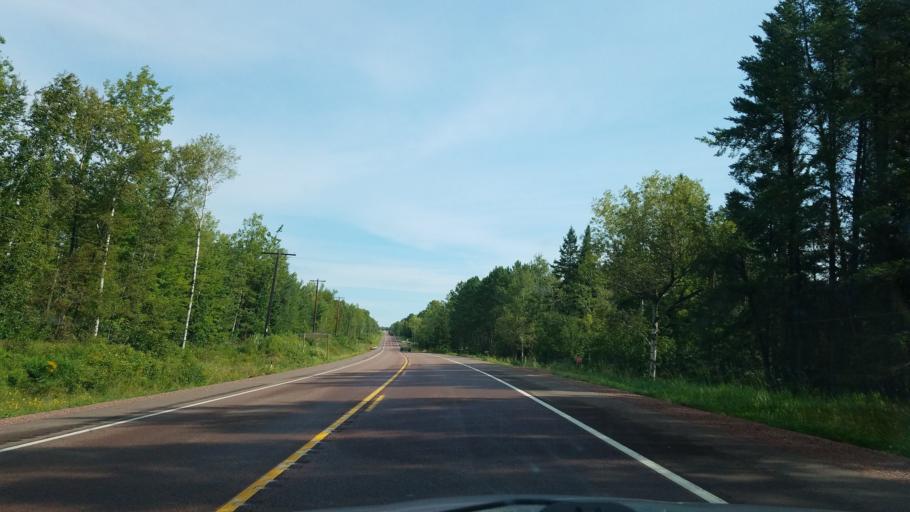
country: US
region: Wisconsin
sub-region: Ashland County
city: Ashland
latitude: 46.6074
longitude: -90.9470
